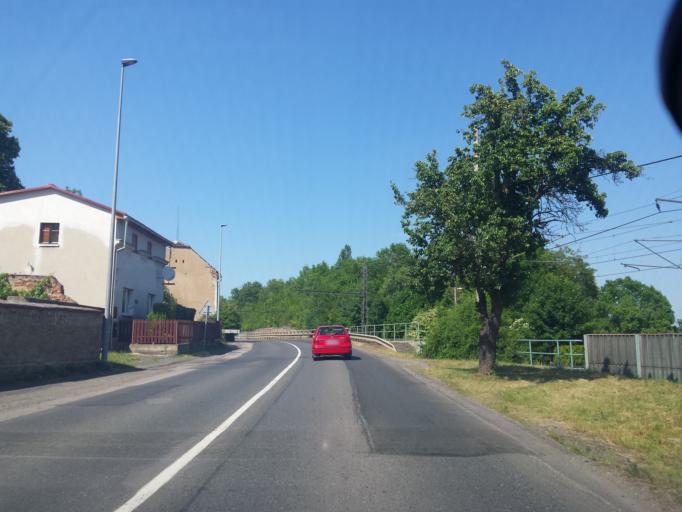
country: CZ
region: Central Bohemia
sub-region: Okres Melnik
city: Veltrusy
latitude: 50.3030
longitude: 14.3169
